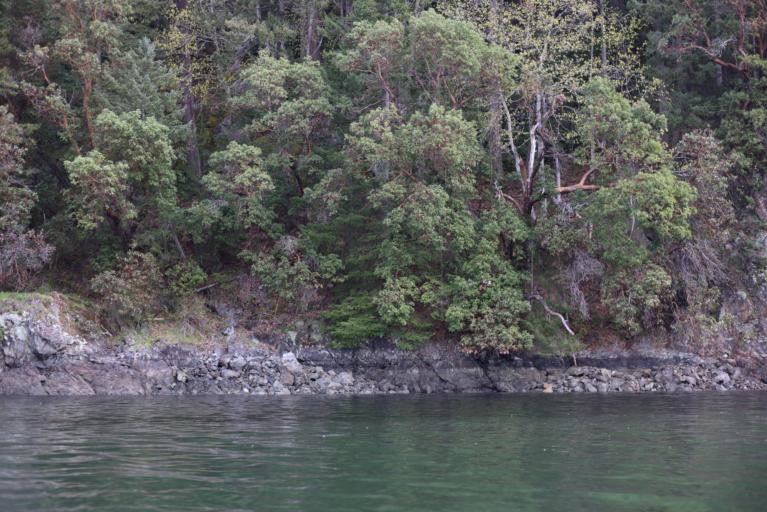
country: CA
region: British Columbia
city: Langford
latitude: 48.5299
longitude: -123.5367
